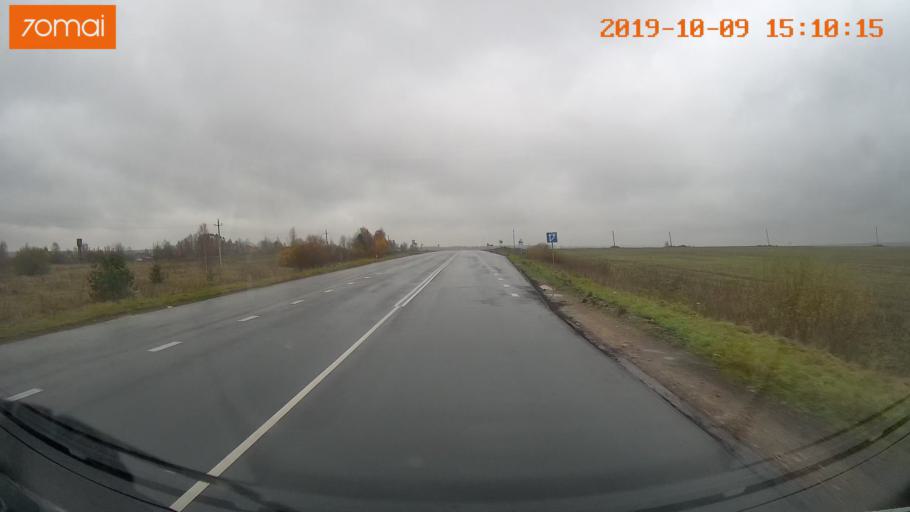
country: RU
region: Kostroma
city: Susanino
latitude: 58.1803
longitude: 41.6427
